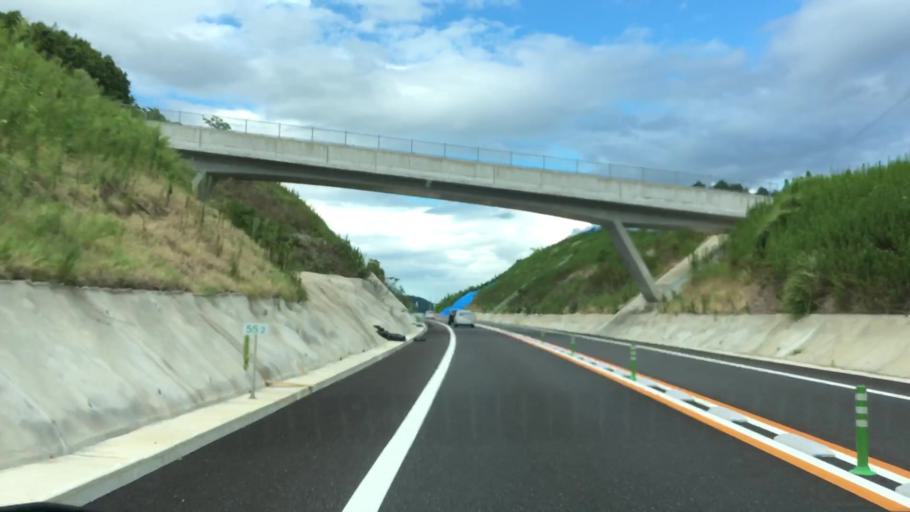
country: JP
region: Saga Prefecture
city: Imaricho-ko
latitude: 33.3208
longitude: 129.9257
